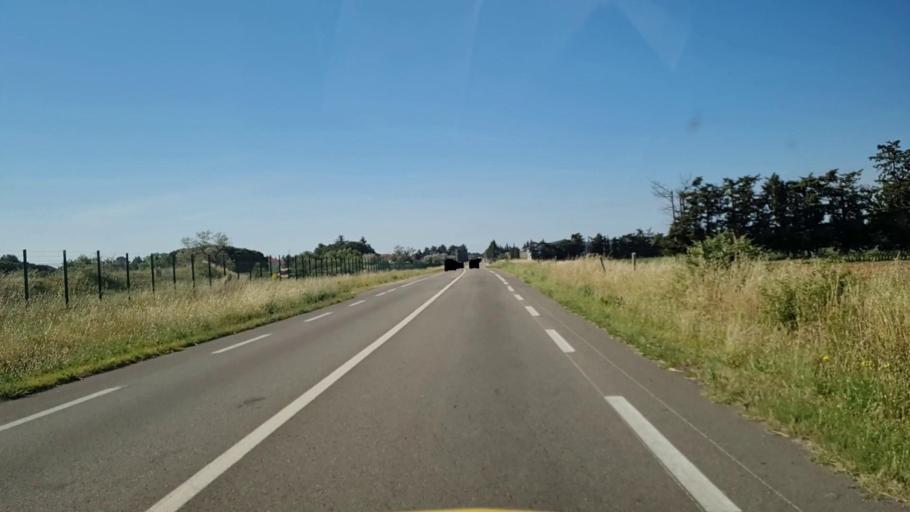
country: FR
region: Languedoc-Roussillon
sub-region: Departement du Gard
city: Garons
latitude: 43.7682
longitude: 4.4054
